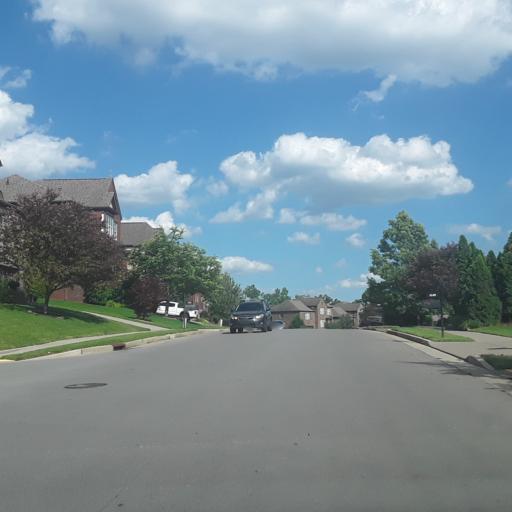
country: US
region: Tennessee
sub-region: Davidson County
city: Lakewood
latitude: 36.1902
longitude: -86.6364
